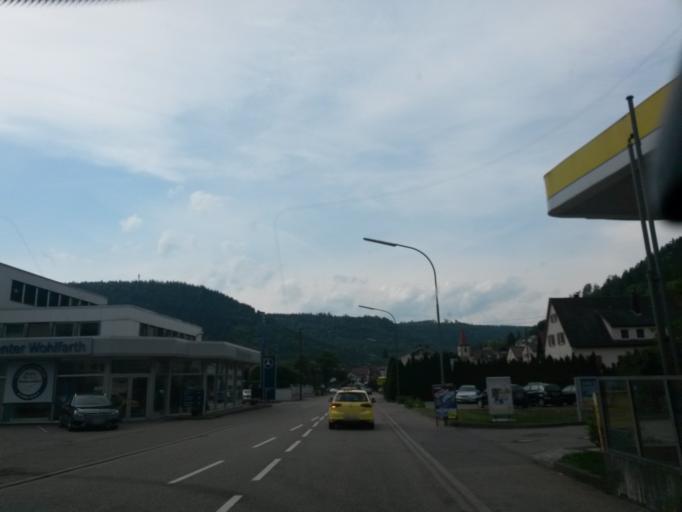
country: DE
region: Baden-Wuerttemberg
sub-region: Karlsruhe Region
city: Hofen an der Enz
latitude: 48.7713
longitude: 8.5837
